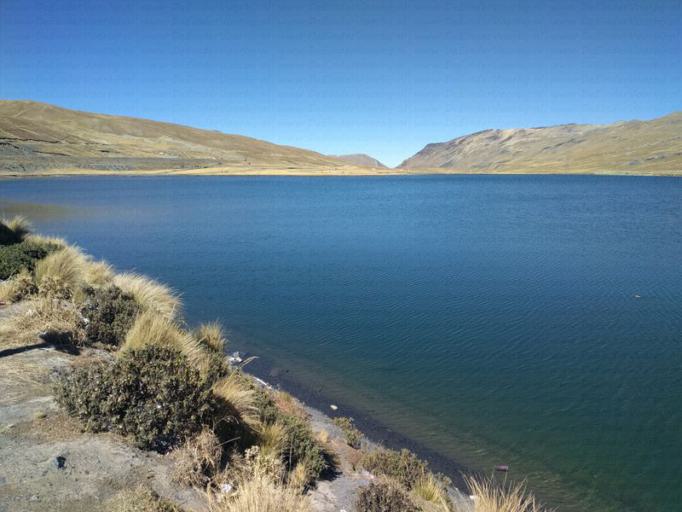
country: BO
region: La Paz
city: La Paz
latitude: -16.3385
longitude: -68.0406
